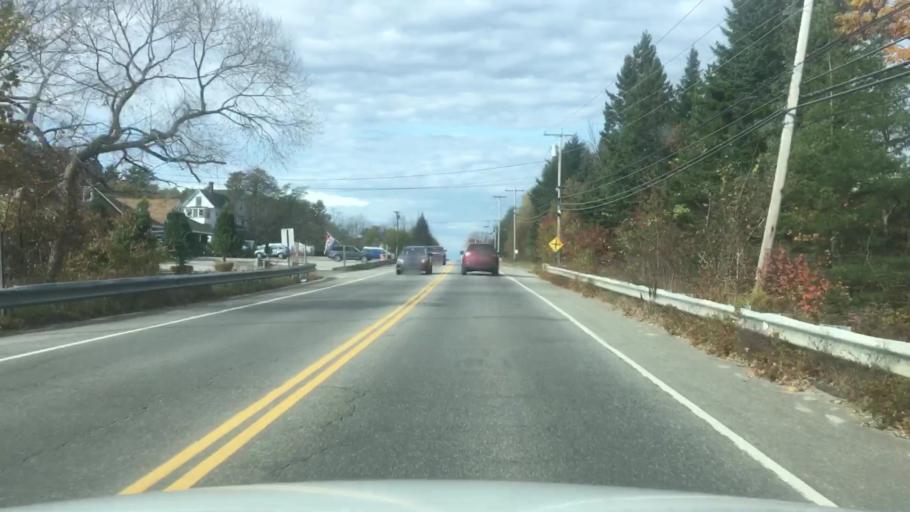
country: US
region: Maine
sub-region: Sagadahoc County
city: Bath
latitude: 43.9124
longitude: -69.8745
